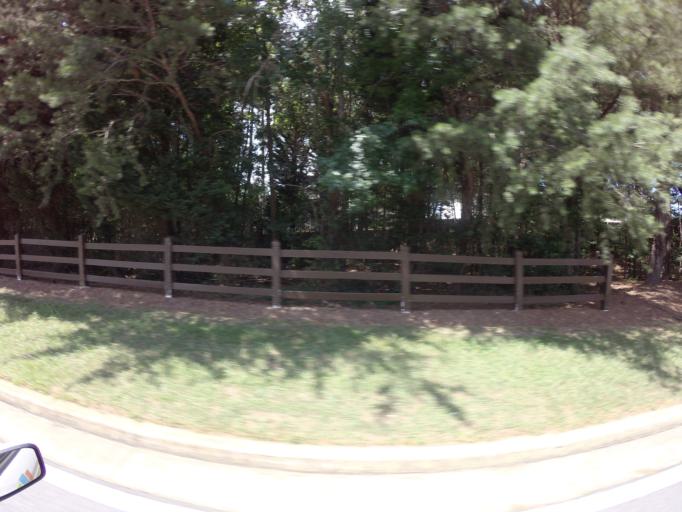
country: US
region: Georgia
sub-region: Fulton County
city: Johns Creek
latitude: 34.0082
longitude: -84.2113
